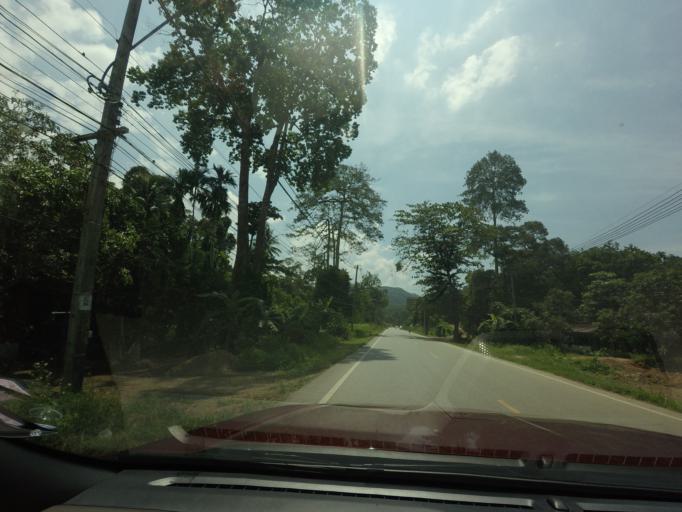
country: TH
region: Yala
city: Betong
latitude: 5.8116
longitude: 101.0838
